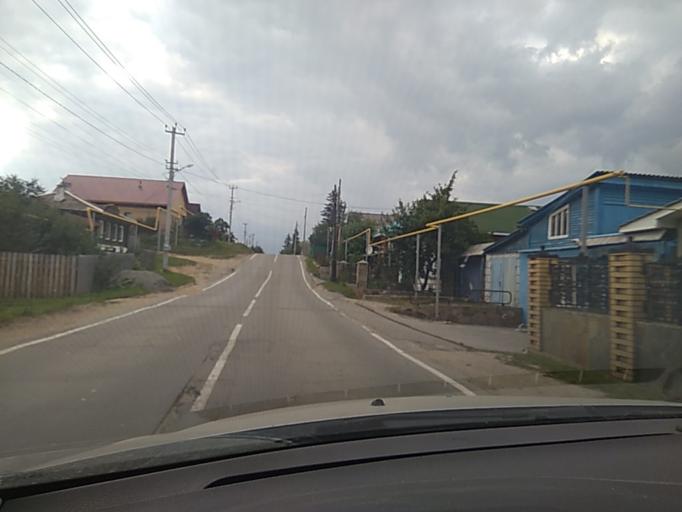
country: RU
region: Chelyabinsk
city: Kyshtym
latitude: 55.6988
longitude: 60.5368
